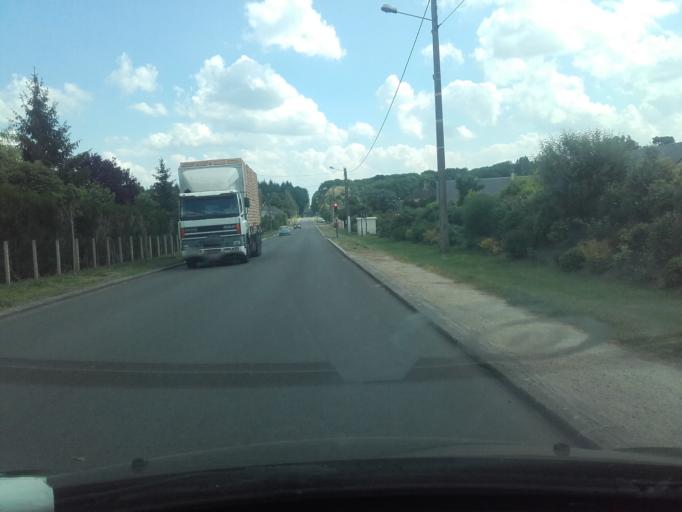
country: FR
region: Centre
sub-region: Departement d'Indre-et-Loire
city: Mazieres-de-Touraine
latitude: 47.3818
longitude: 0.4239
